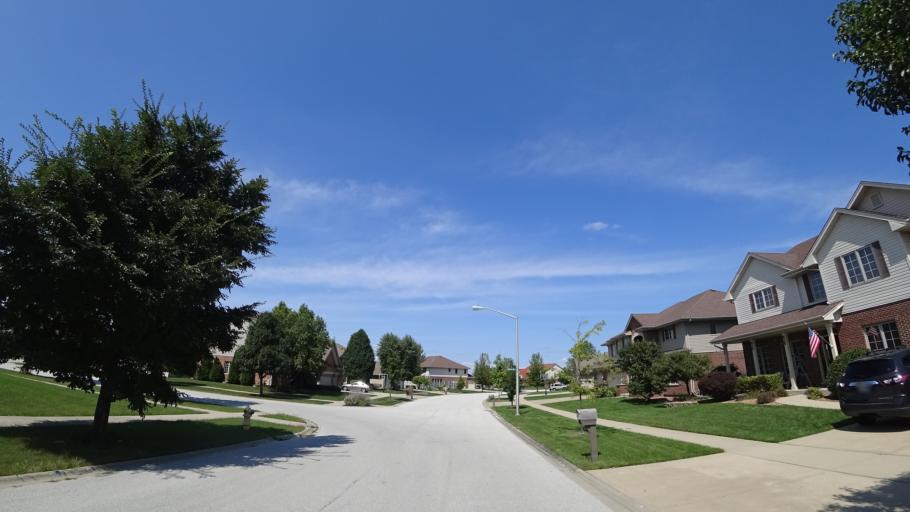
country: US
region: Illinois
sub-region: Cook County
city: Orland Hills
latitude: 41.5606
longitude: -87.8311
